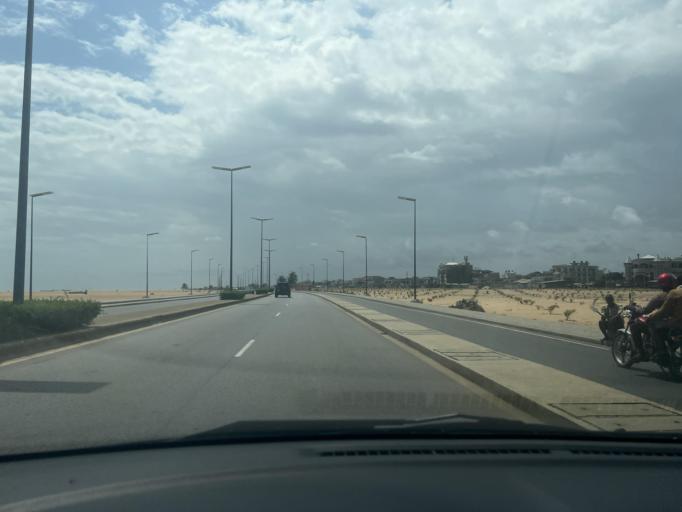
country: BJ
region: Littoral
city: Cotonou
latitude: 6.3487
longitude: 2.3725
